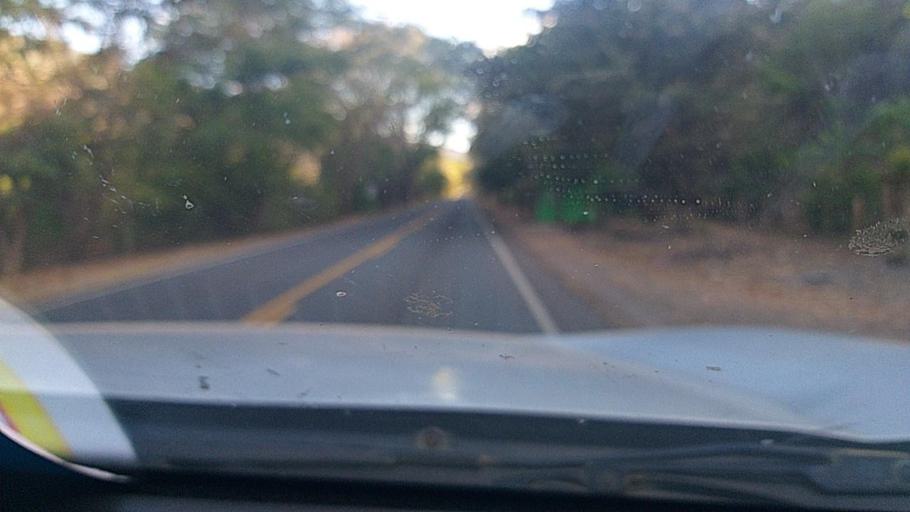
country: NI
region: Esteli
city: Condega
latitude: 13.2978
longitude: -86.3492
